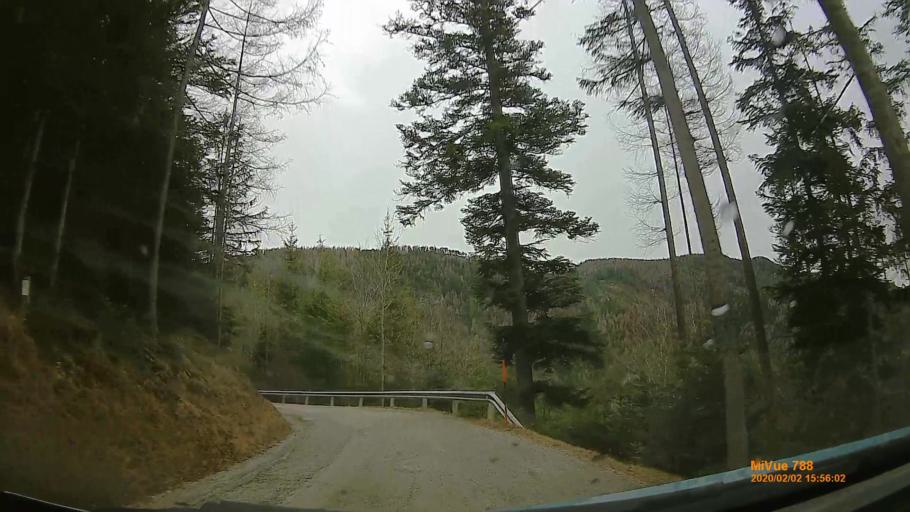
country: AT
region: Lower Austria
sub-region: Politischer Bezirk Neunkirchen
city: Semmering
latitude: 47.6686
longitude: 15.7837
